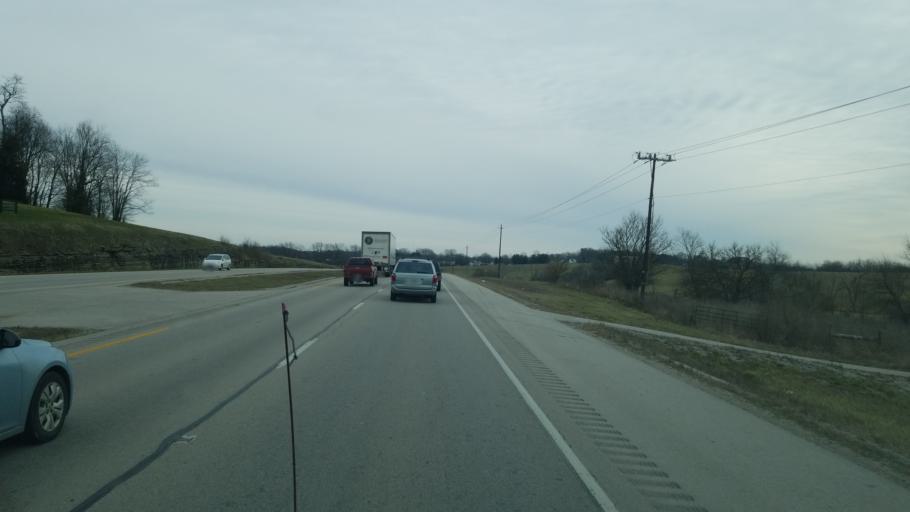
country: US
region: Kentucky
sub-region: Bourbon County
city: Paris
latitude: 38.2257
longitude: -84.2683
